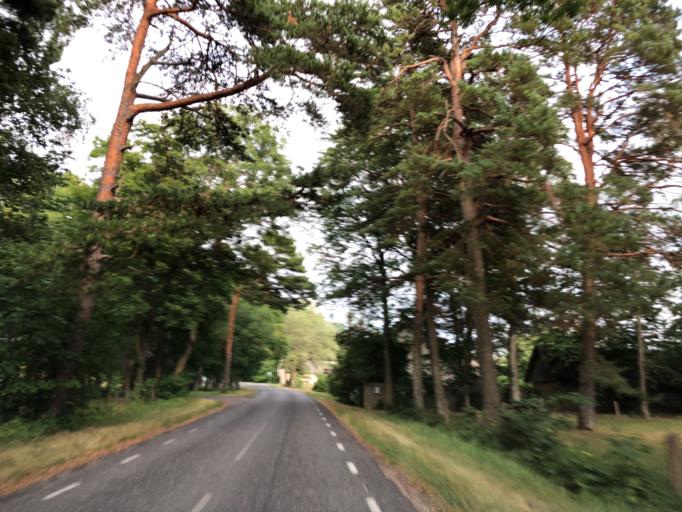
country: EE
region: Hiiumaa
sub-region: Kaerdla linn
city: Kardla
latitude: 58.7890
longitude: 22.8271
